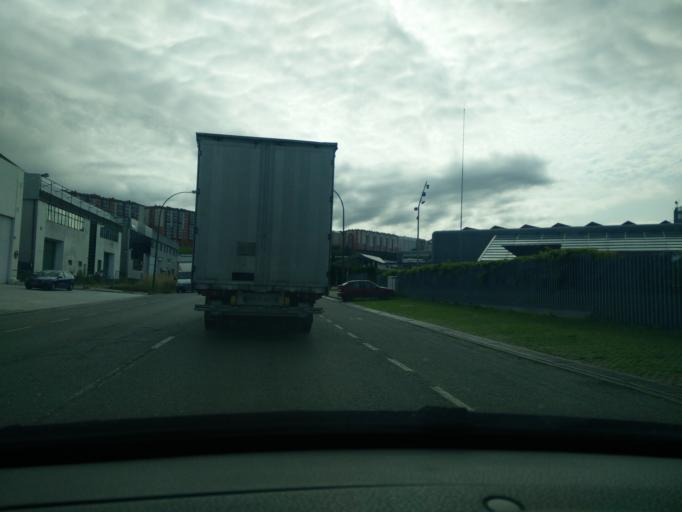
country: ES
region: Galicia
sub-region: Provincia da Coruna
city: A Coruna
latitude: 43.3297
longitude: -8.4317
